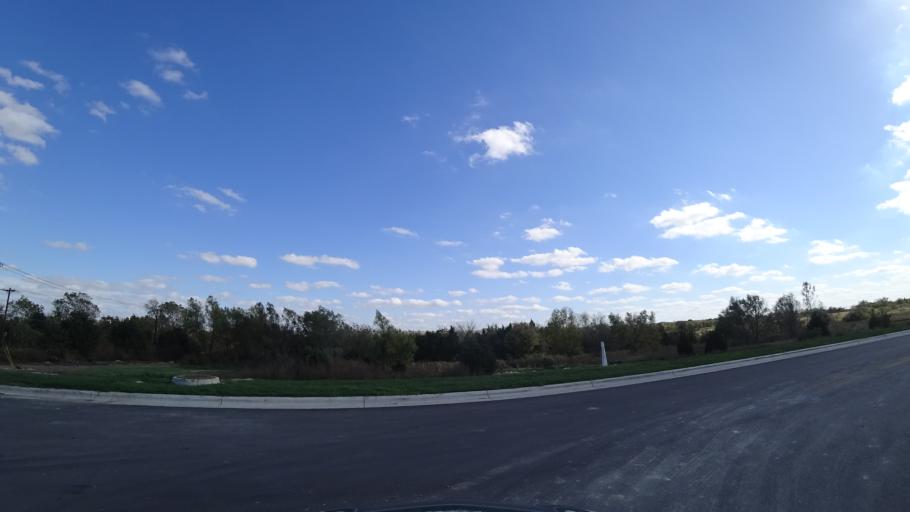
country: US
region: Texas
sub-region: Travis County
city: Wells Branch
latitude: 30.4661
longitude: -97.6772
